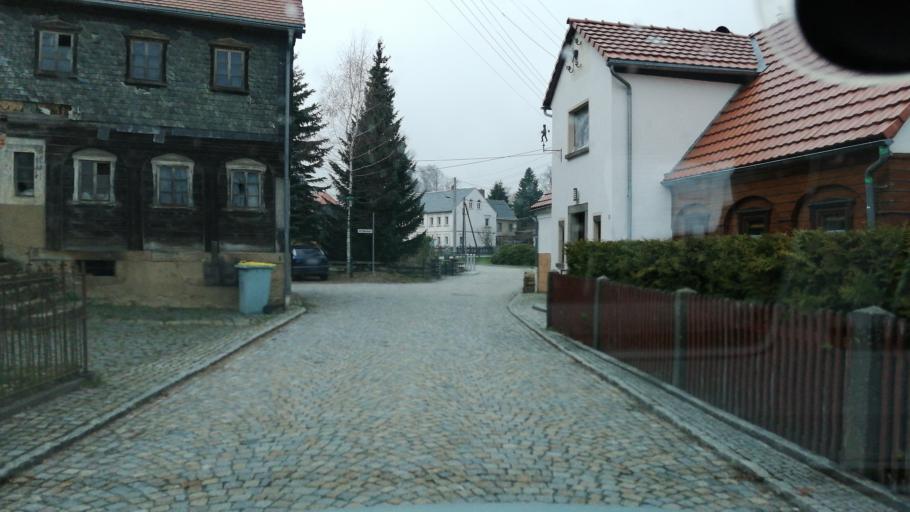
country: DE
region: Saxony
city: Schonbach
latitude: 51.0612
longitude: 14.5752
